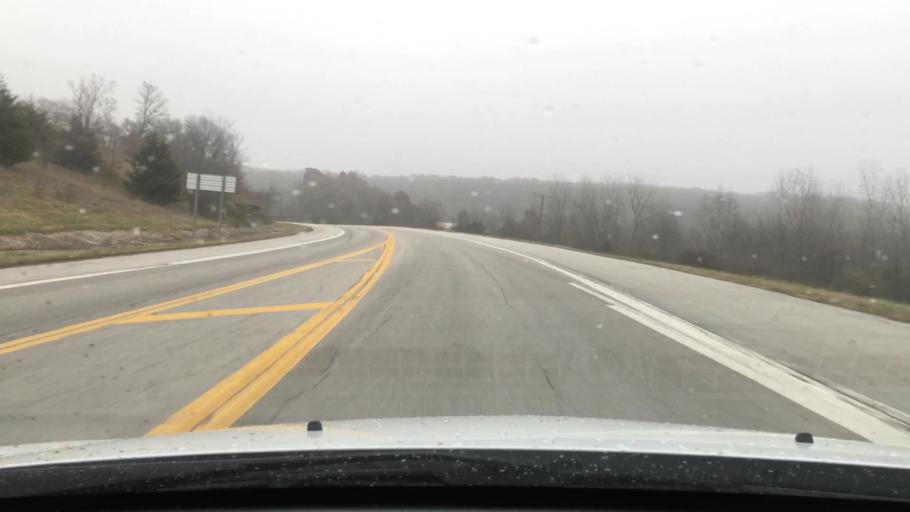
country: US
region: Missouri
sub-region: Pike County
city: Bowling Green
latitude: 39.3625
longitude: -91.1853
